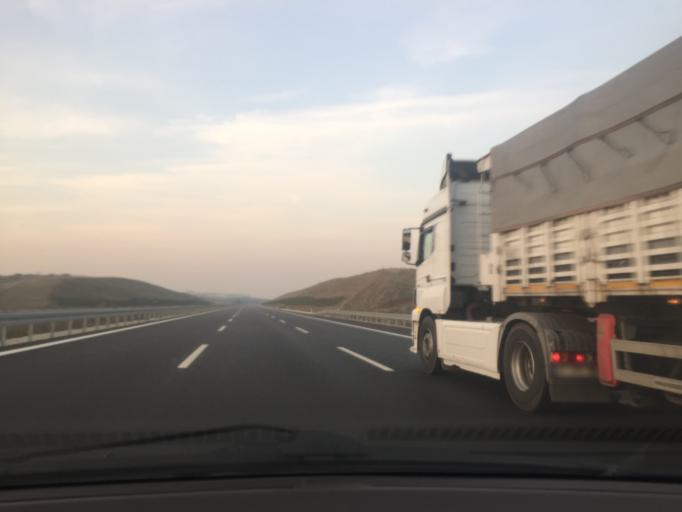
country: TR
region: Bursa
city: Karacabey
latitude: 40.2640
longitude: 28.4881
